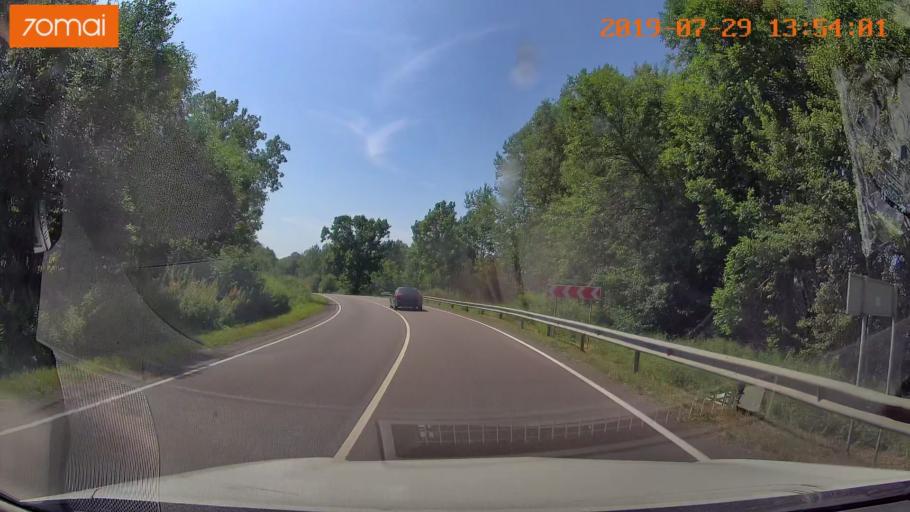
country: RU
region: Kaliningrad
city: Primorsk
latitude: 54.7265
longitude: 19.9710
